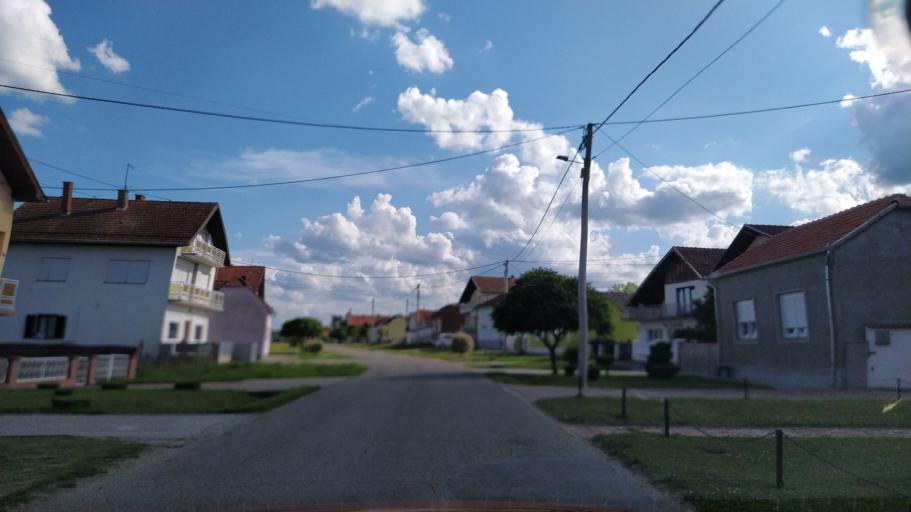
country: HR
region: Virovitick-Podravska
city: Pitomaca
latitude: 45.9623
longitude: 17.2158
